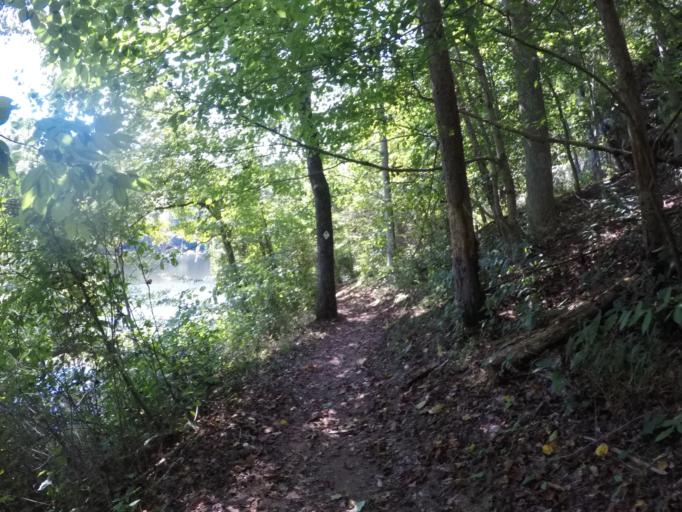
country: US
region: Ohio
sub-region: Lawrence County
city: Ironton
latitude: 38.6098
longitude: -82.6276
